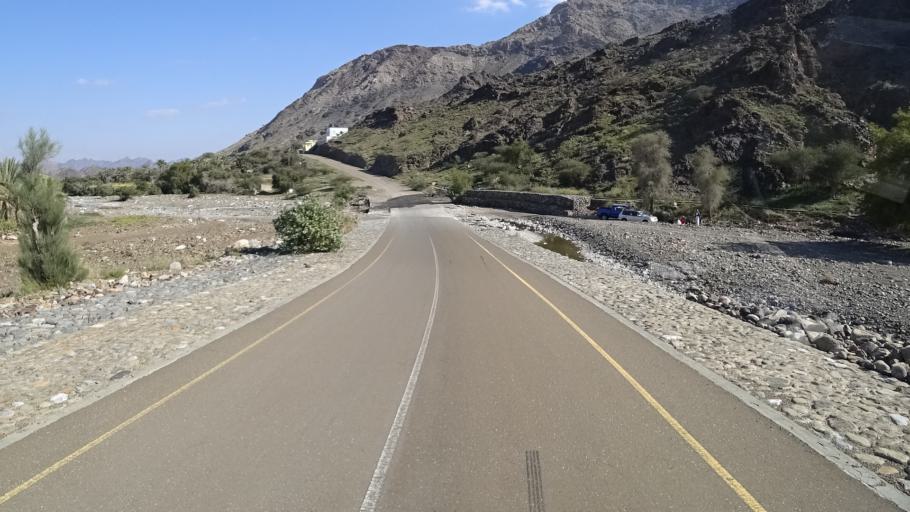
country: OM
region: Al Batinah
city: Rustaq
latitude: 23.4584
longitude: 57.0823
